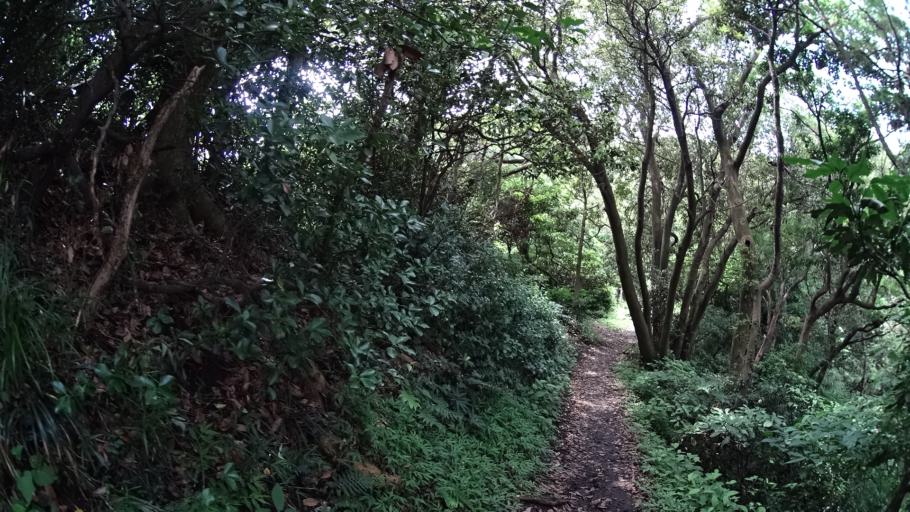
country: JP
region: Kanagawa
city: Yokosuka
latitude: 35.2180
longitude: 139.6648
